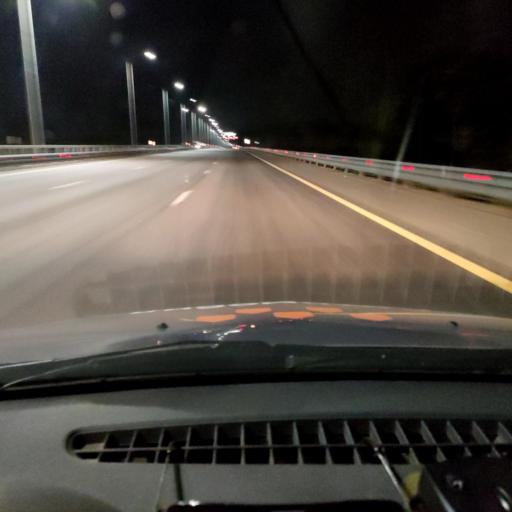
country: RU
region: Voronezj
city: Podgornoye
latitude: 51.8354
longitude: 39.2280
